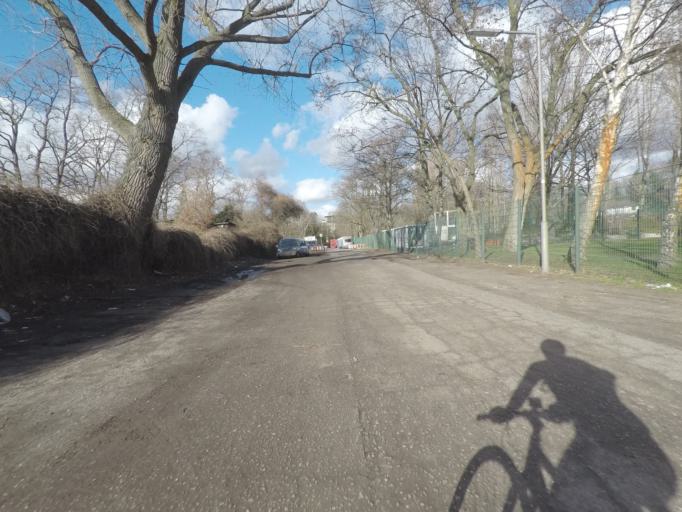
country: DE
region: Berlin
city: Bezirk Kreuzberg
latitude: 52.4838
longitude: 13.4065
